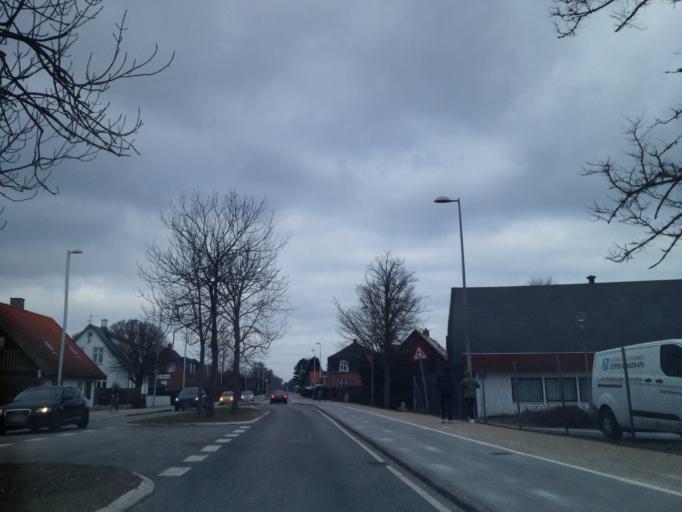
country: DK
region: Capital Region
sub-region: Fredensborg Kommune
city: Humlebaek
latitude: 55.9575
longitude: 12.5308
